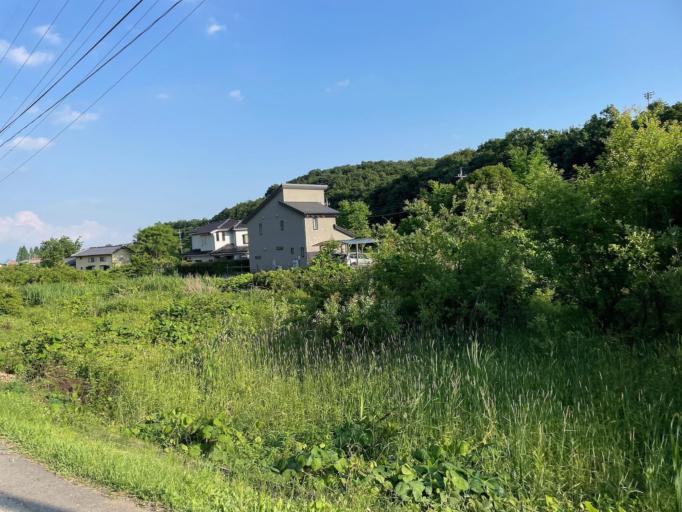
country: JP
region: Saitama
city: Sakado
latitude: 36.0057
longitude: 139.3712
